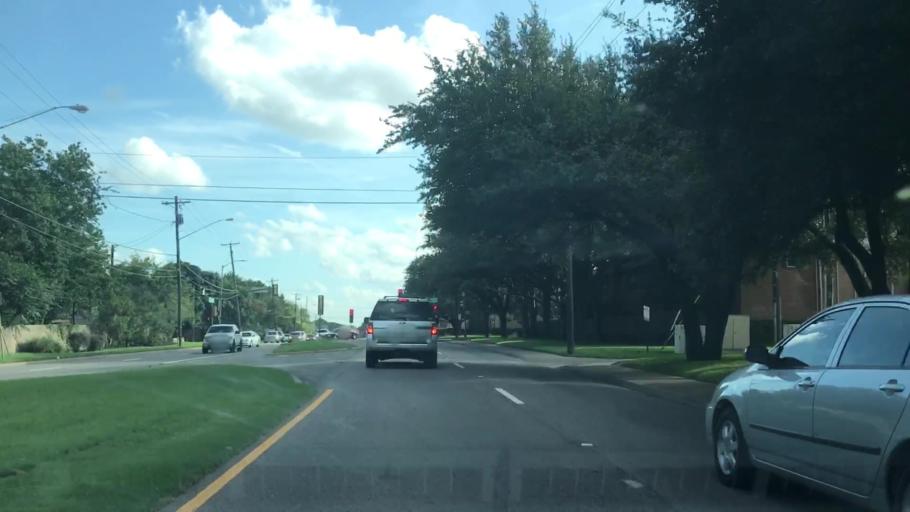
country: US
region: Texas
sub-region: Dallas County
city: Highland Park
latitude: 32.8475
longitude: -96.7614
